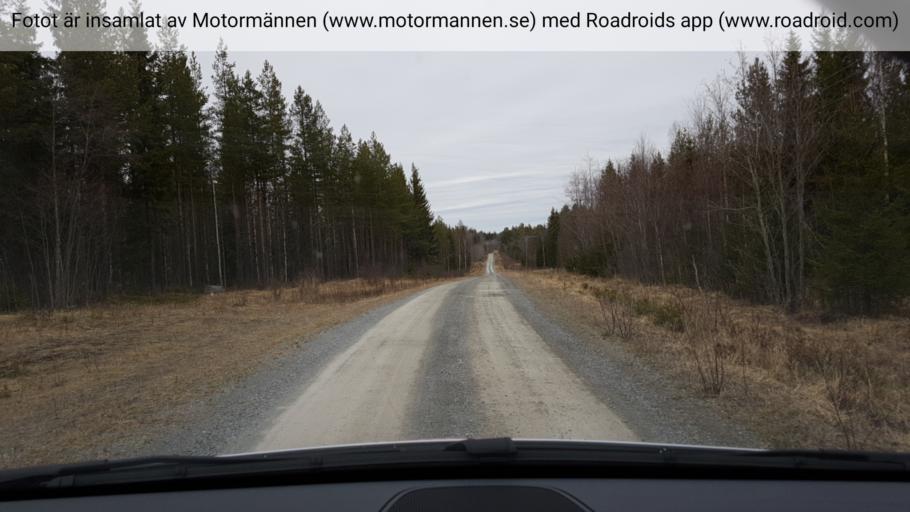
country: SE
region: Jaemtland
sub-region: Bergs Kommun
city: Hoverberg
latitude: 62.8608
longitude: 14.6134
